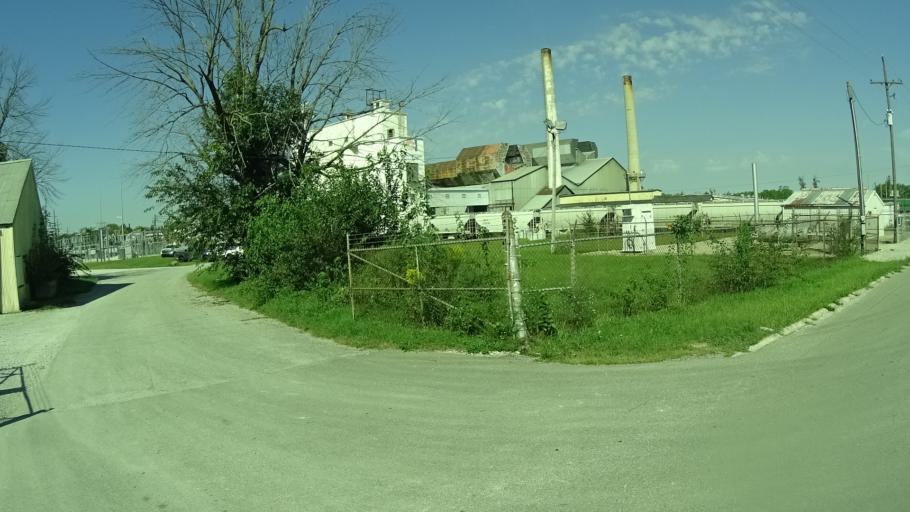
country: US
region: Indiana
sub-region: Madison County
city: Lapel
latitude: 40.0661
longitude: -85.8535
